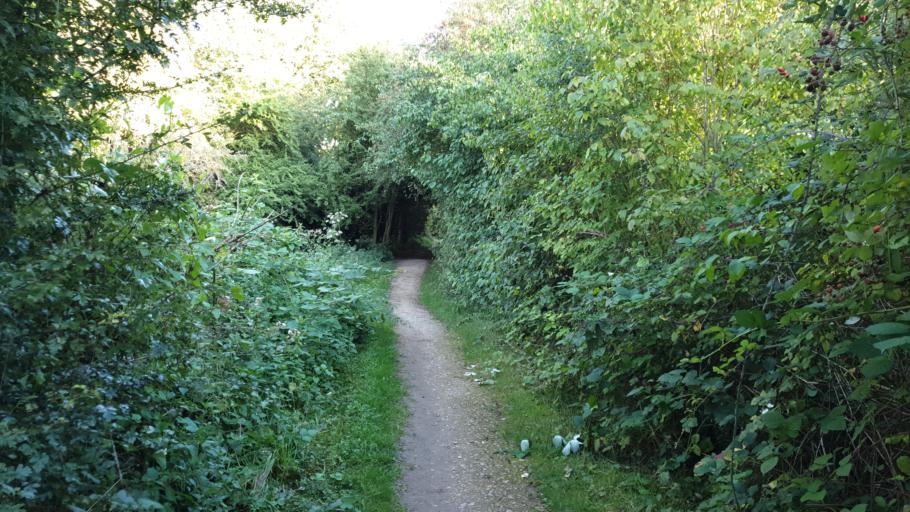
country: GB
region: England
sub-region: Wiltshire
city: Minety
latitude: 51.6457
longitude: -1.9611
